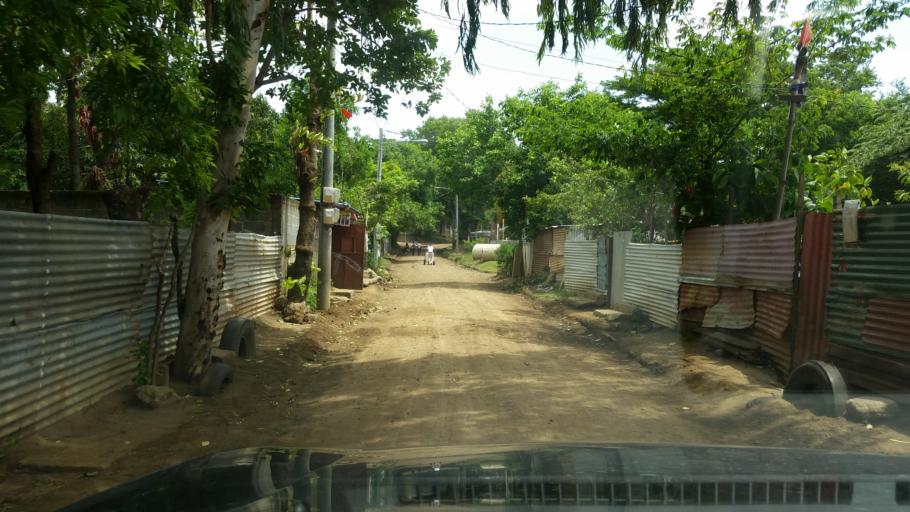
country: NI
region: Managua
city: Managua
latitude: 12.1144
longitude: -86.2216
